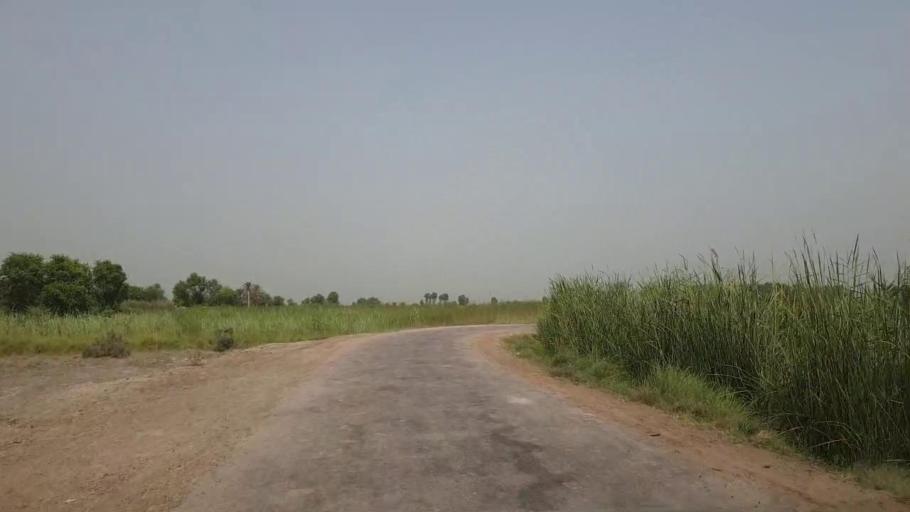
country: PK
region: Sindh
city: Gambat
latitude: 27.4043
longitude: 68.5507
